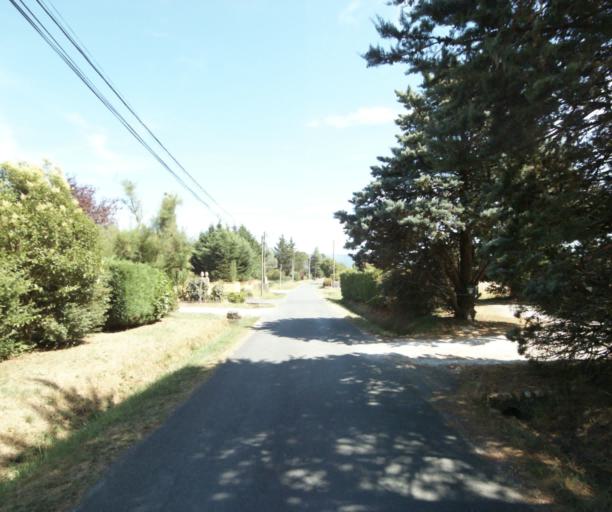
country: FR
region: Midi-Pyrenees
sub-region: Departement du Tarn
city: Puylaurens
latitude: 43.5340
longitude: 2.0159
